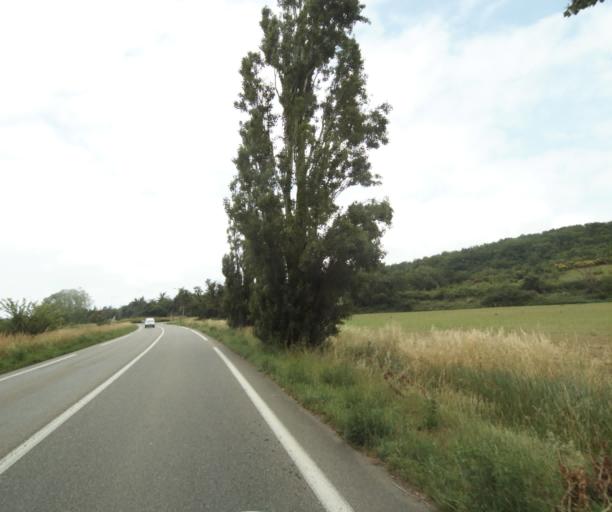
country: FR
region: Midi-Pyrenees
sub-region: Departement du Tarn-et-Garonne
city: Saint-Nauphary
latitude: 43.9892
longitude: 1.3928
